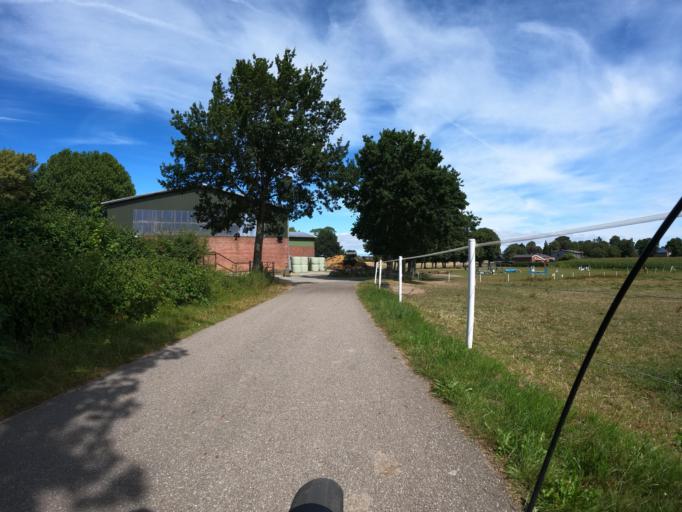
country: DE
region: Schleswig-Holstein
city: Steinbergkirche
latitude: 54.7686
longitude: 9.7607
